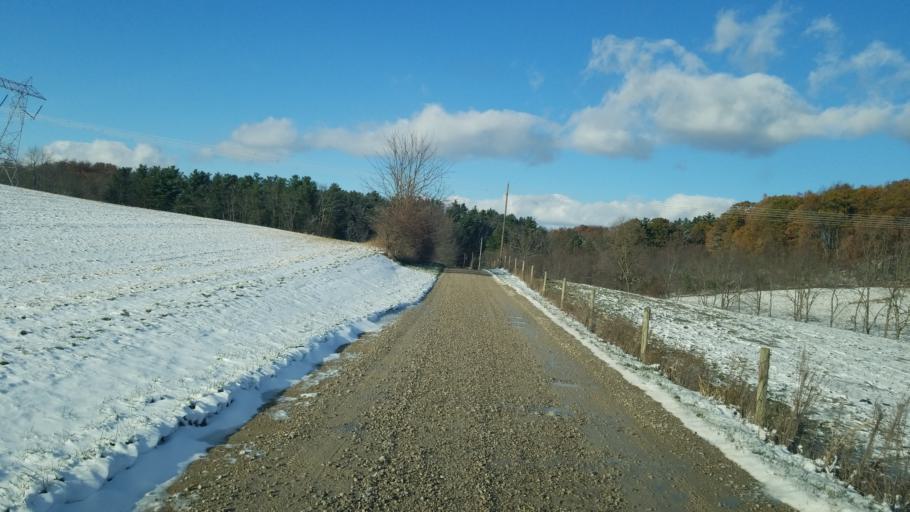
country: US
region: Ohio
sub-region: Licking County
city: Newark
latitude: 40.1503
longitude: -82.3886
